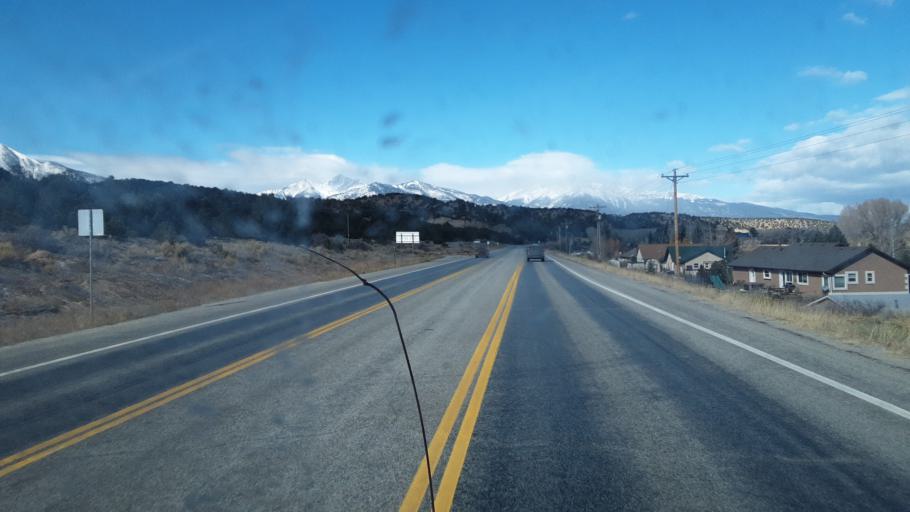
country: US
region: Colorado
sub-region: Chaffee County
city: Buena Vista
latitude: 38.7672
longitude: -106.0983
